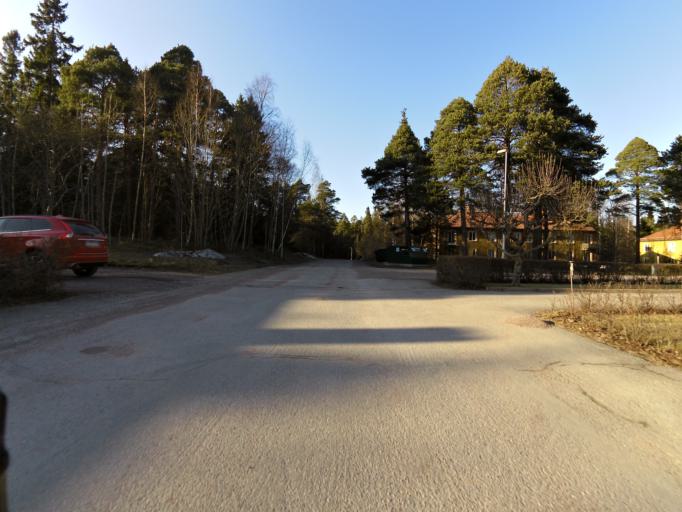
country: SE
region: Gaevleborg
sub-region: Gavle Kommun
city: Gavle
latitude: 60.6833
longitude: 17.2358
